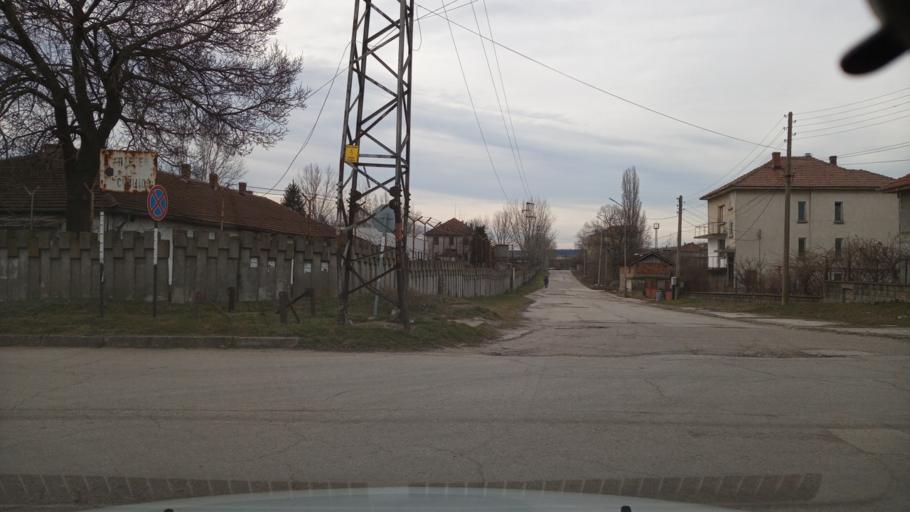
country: BG
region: Pleven
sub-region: Obshtina Belene
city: Belene
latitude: 43.6426
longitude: 25.1202
